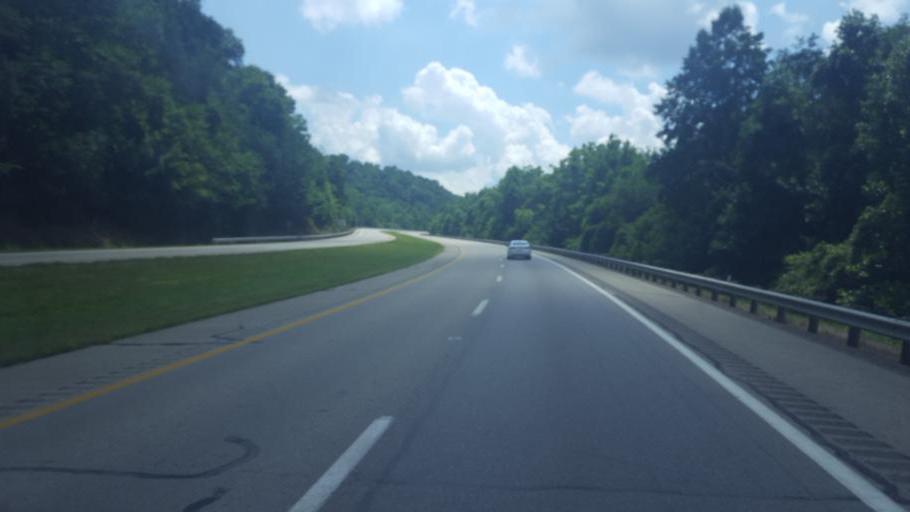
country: US
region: Ohio
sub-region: Jackson County
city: Jackson
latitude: 39.1546
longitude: -82.7326
